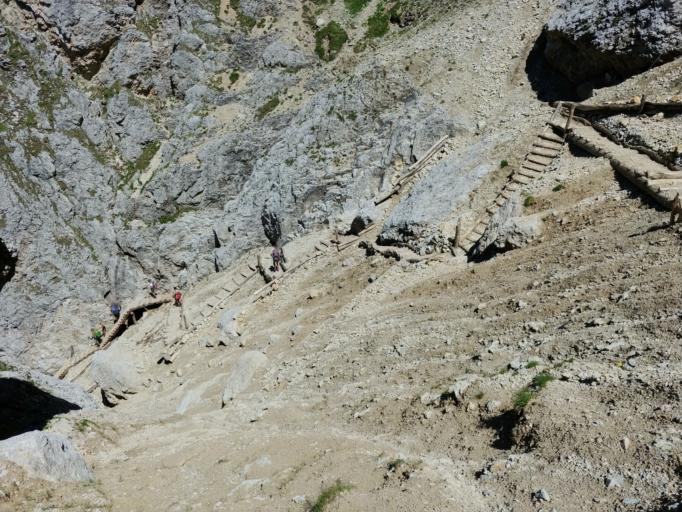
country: IT
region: Trentino-Alto Adige
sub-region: Bolzano
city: Santa Cristina Valgardena
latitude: 46.6019
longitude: 11.7356
